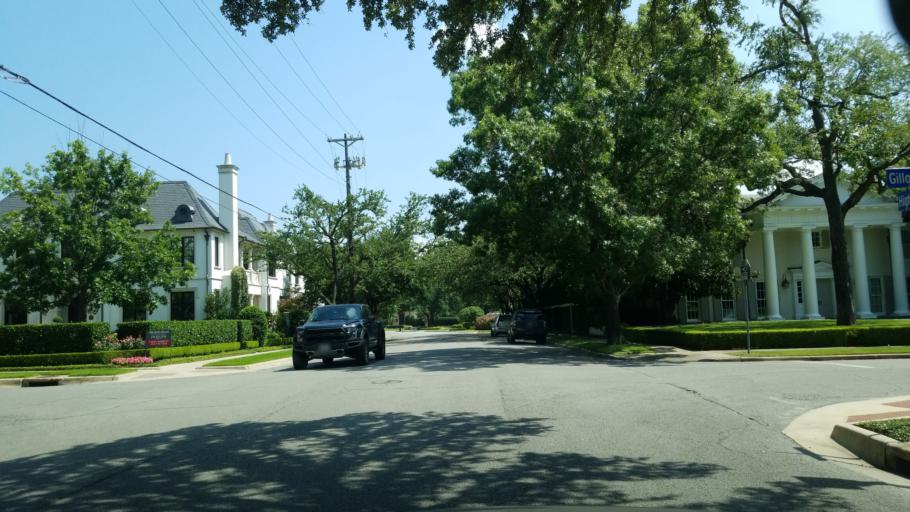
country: US
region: Texas
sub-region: Dallas County
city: Highland Park
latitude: 32.8296
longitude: -96.8002
